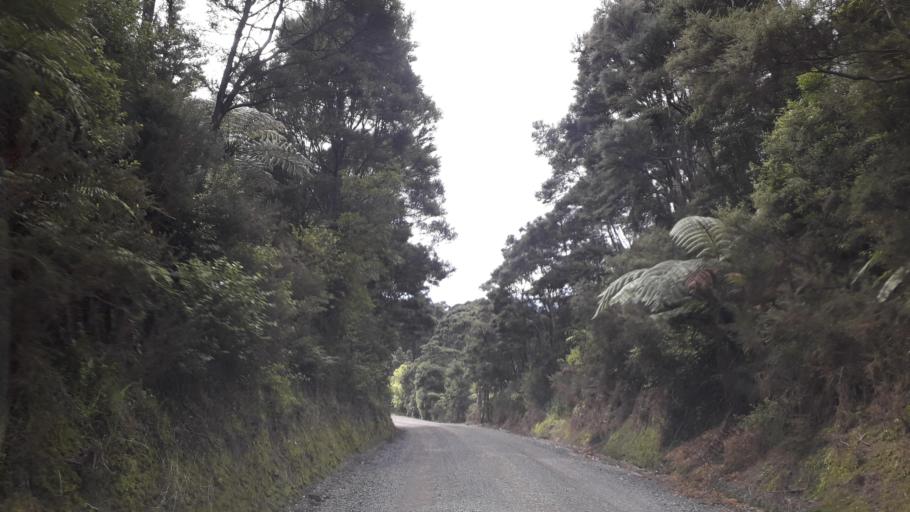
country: NZ
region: Northland
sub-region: Far North District
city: Paihia
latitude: -35.3130
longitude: 174.2242
